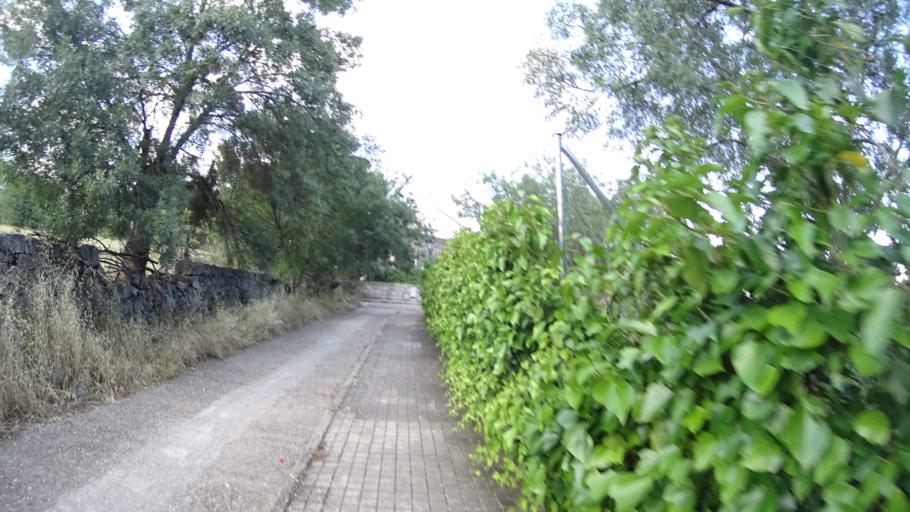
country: ES
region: Madrid
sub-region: Provincia de Madrid
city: Hoyo de Manzanares
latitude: 40.6265
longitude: -3.9057
